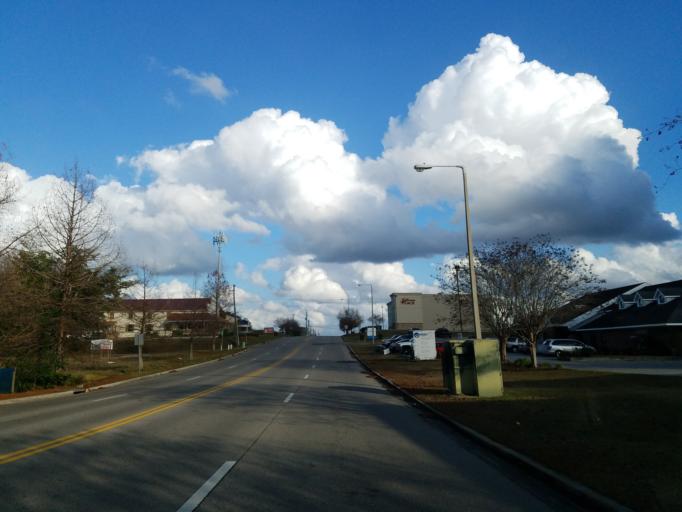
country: US
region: Mississippi
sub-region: Jones County
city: Laurel
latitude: 31.6860
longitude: -89.1451
